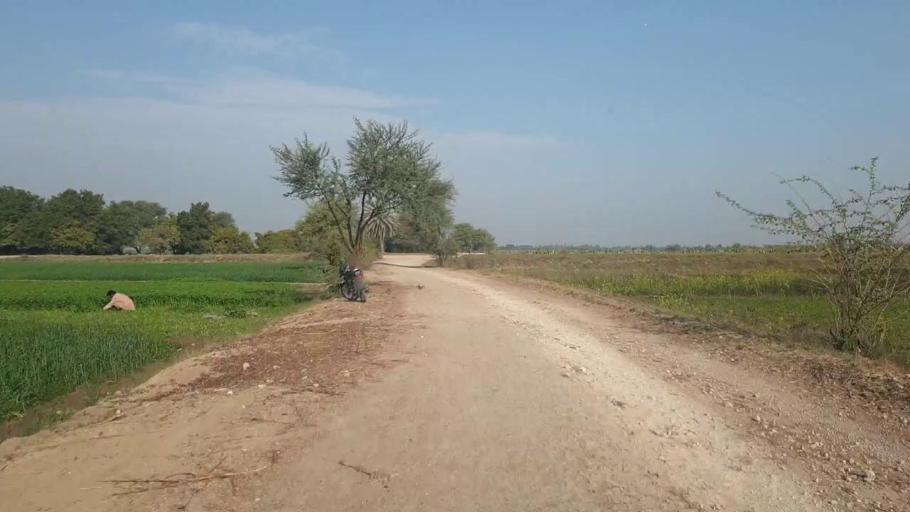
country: PK
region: Sindh
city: Tando Adam
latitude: 25.7524
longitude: 68.6072
